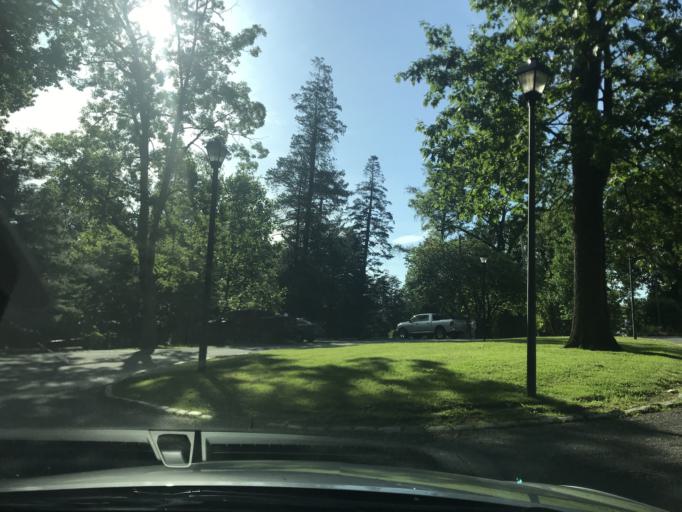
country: US
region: Maryland
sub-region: Harford County
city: North Bel Air
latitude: 39.5348
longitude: -76.3608
